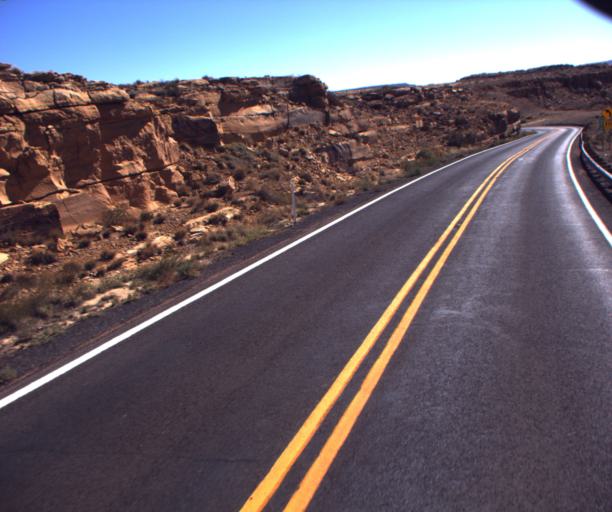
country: US
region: Arizona
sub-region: Navajo County
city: First Mesa
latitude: 35.8815
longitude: -110.6267
